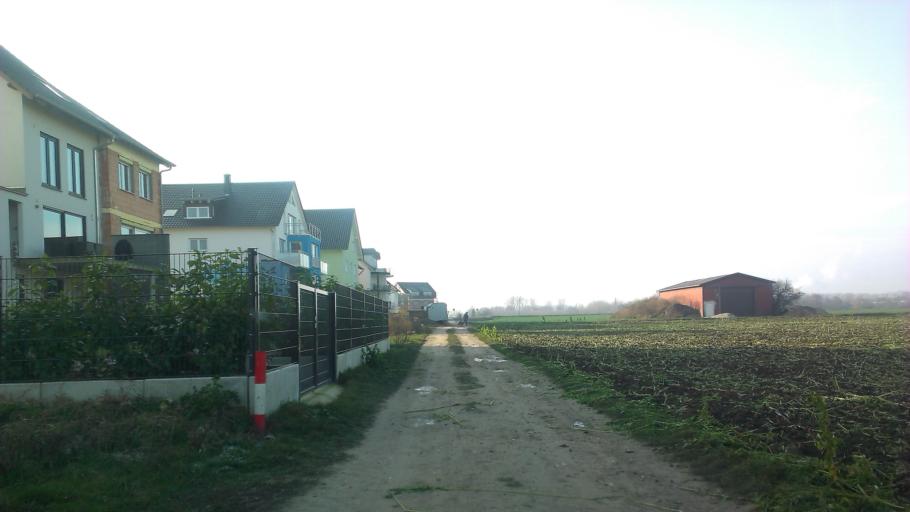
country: DE
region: Hesse
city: Lampertheim
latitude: 49.5496
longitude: 8.4411
